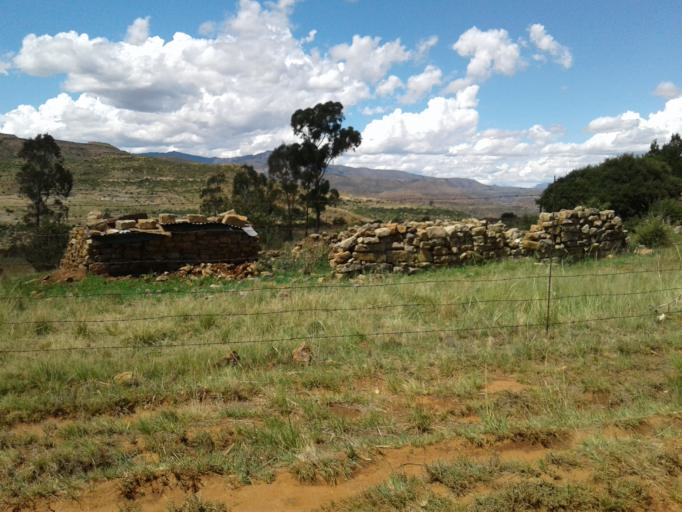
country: LS
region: Quthing
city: Quthing
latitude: -30.3732
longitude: 27.5537
